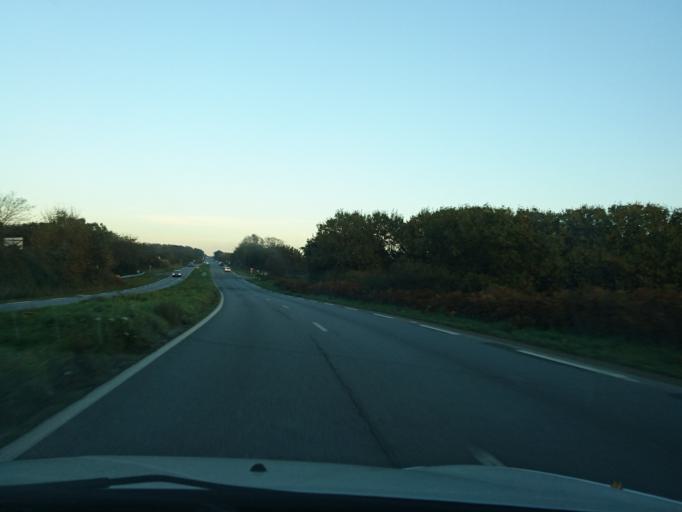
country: FR
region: Brittany
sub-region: Departement du Finistere
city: Saint-Renan
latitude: 48.4274
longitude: -4.5939
